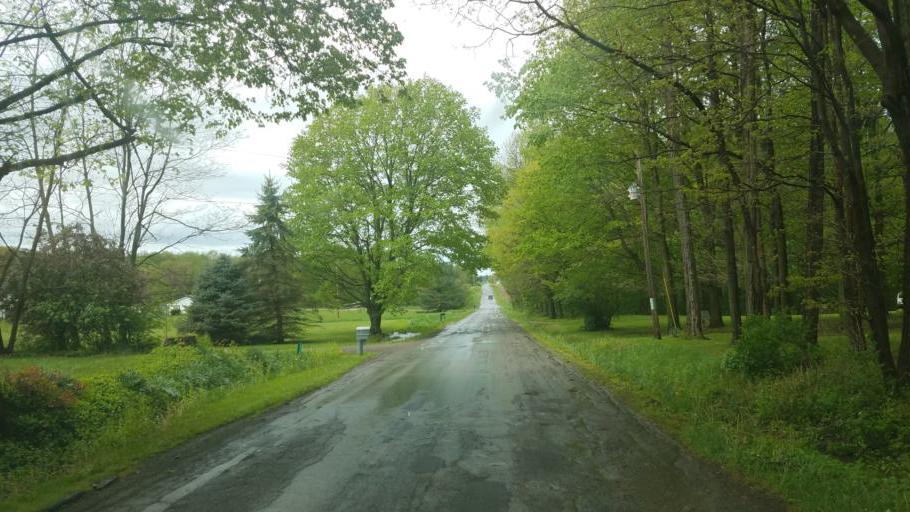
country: US
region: Ohio
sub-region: Richland County
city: Lexington
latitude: 40.6011
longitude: -82.6312
